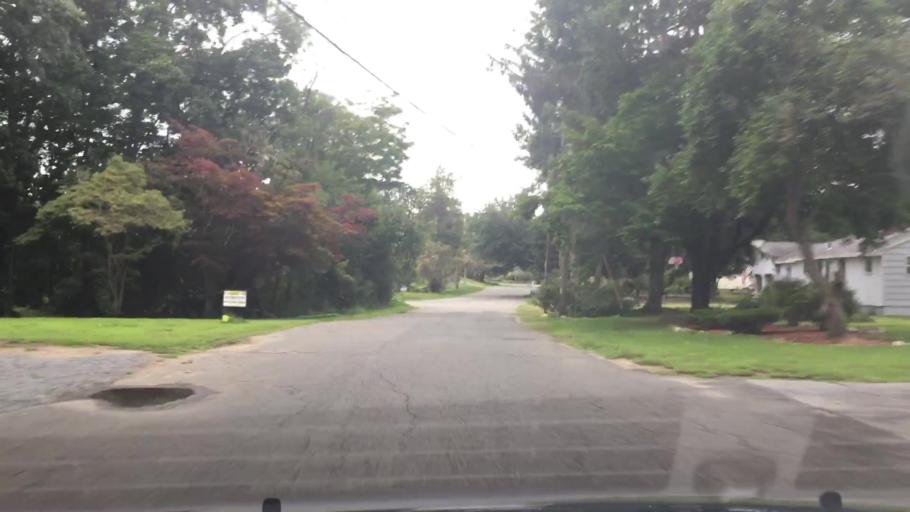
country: US
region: Massachusetts
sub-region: Essex County
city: North Andover
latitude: 42.6810
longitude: -71.0966
